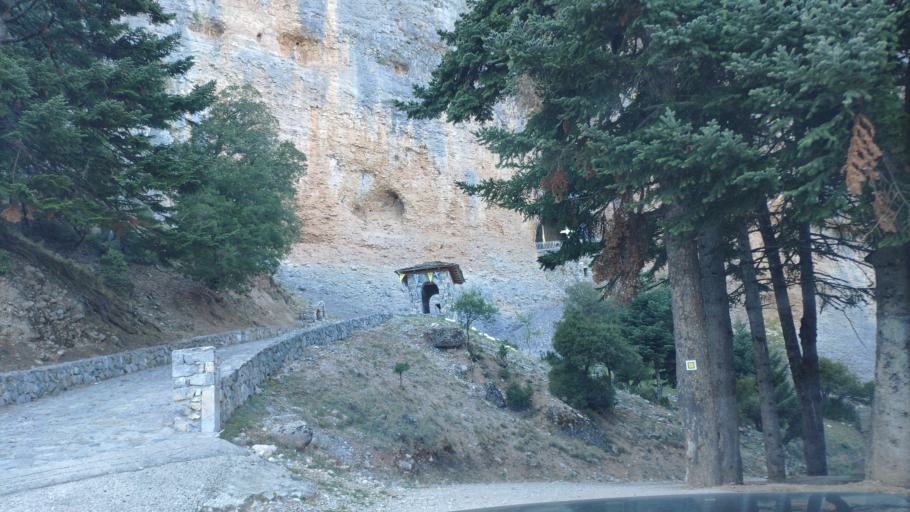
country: GR
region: West Greece
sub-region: Nomos Achaias
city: Aiyira
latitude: 37.9829
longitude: 22.3425
